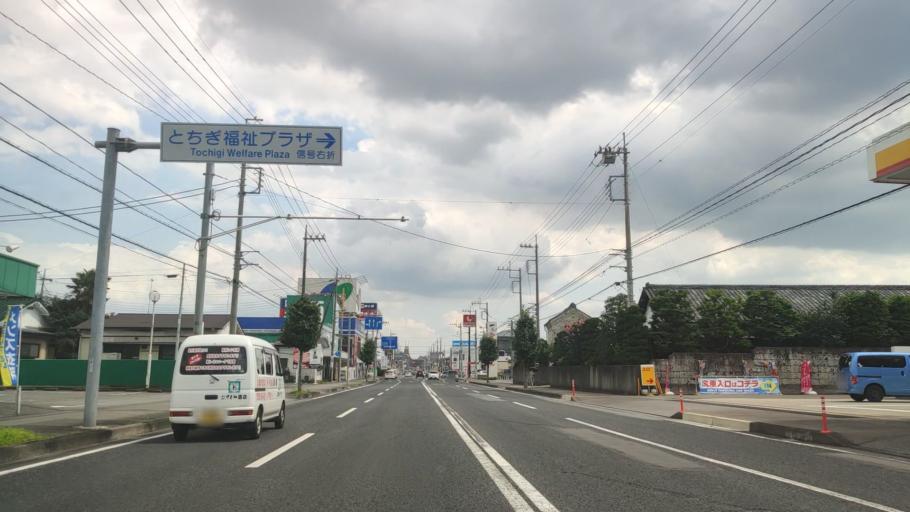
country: JP
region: Tochigi
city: Utsunomiya-shi
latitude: 36.5873
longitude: 139.8651
